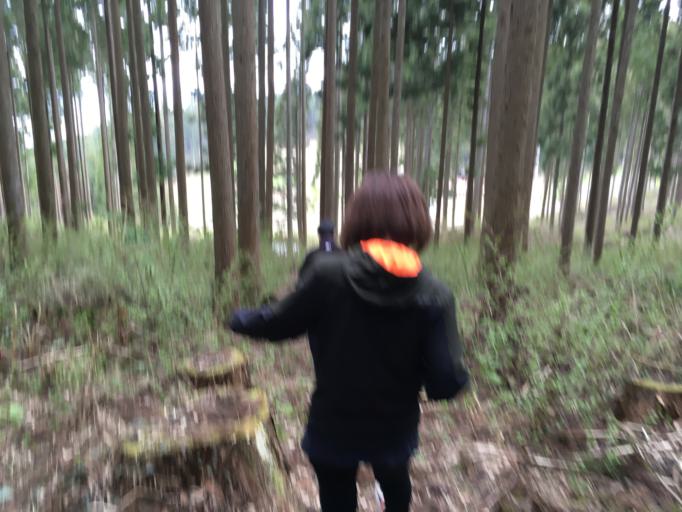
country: JP
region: Iwate
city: Ichinoseki
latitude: 38.9833
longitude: 141.1691
